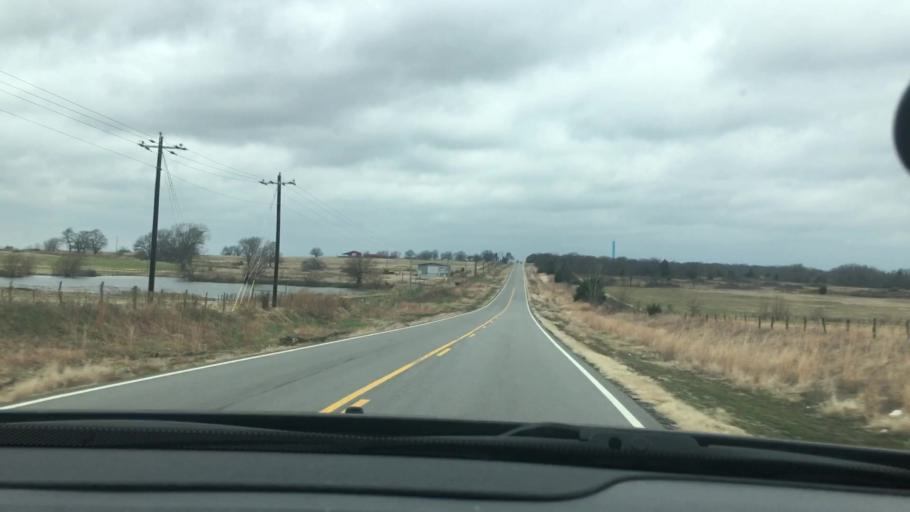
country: US
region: Oklahoma
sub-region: Atoka County
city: Atoka
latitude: 34.3749
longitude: -96.2378
